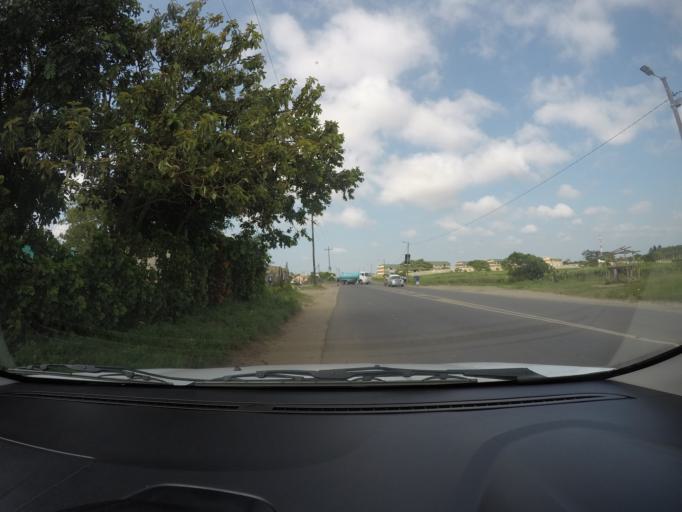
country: ZA
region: KwaZulu-Natal
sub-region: uThungulu District Municipality
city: eSikhawini
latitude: -28.8809
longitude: 31.9065
